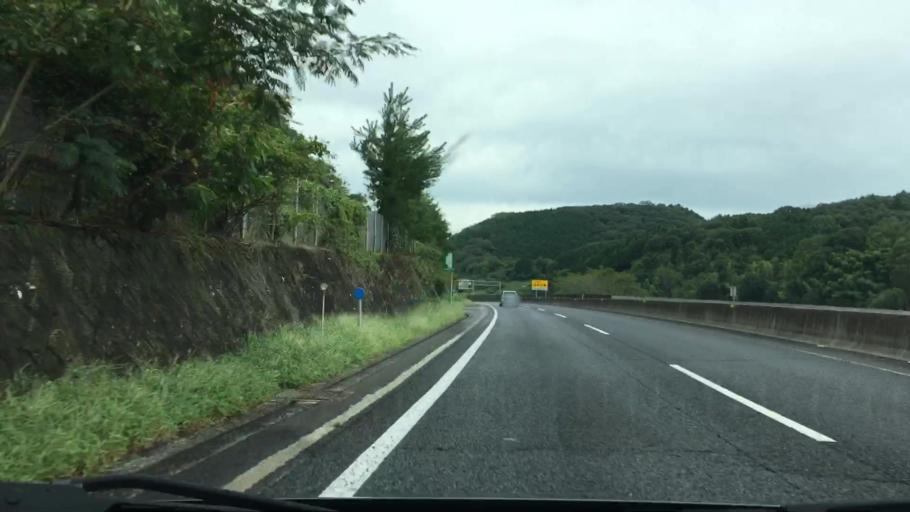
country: JP
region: Hyogo
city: Yamazakicho-nakabirose
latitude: 35.0318
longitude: 134.3996
